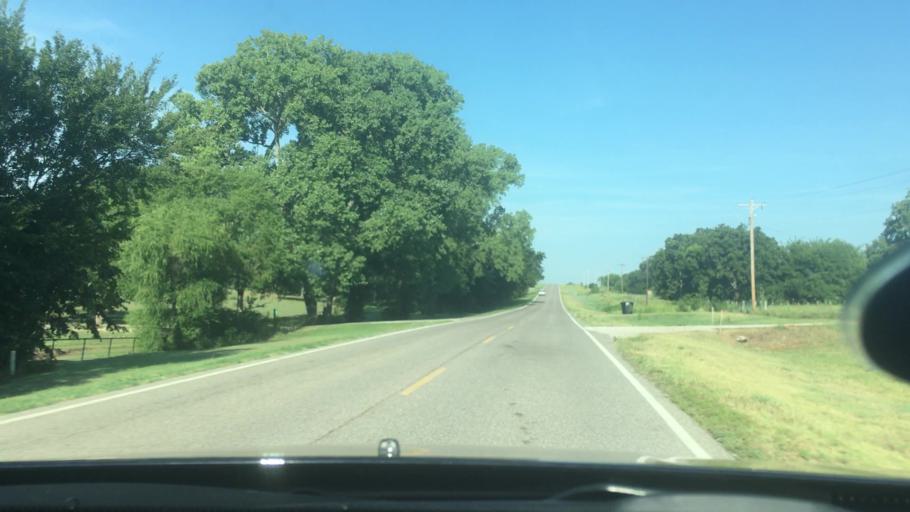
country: US
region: Oklahoma
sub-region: Garvin County
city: Pauls Valley
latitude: 34.6518
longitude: -97.2739
